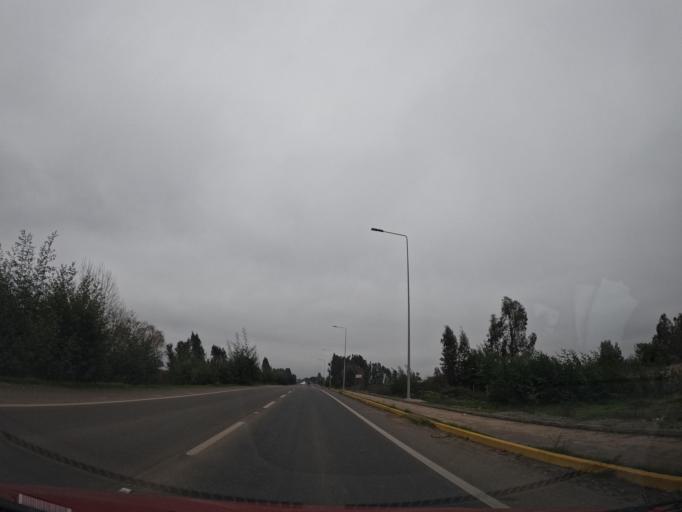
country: CL
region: Maule
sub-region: Provincia de Talca
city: San Clemente
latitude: -35.5200
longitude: -71.4919
